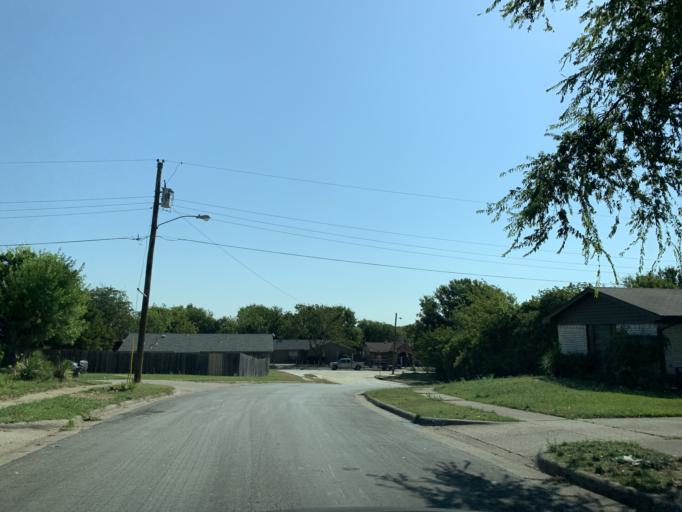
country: US
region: Texas
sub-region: Dallas County
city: Hutchins
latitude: 32.6668
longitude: -96.7541
